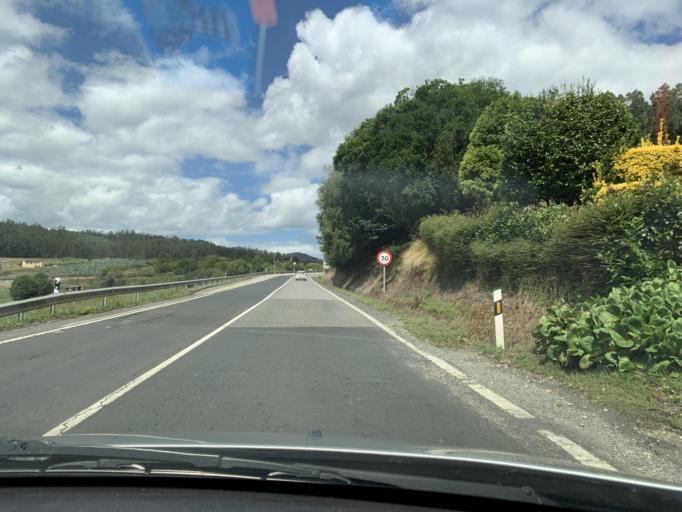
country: ES
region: Galicia
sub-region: Provincia de Lugo
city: Barreiros
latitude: 43.4833
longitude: -7.2912
